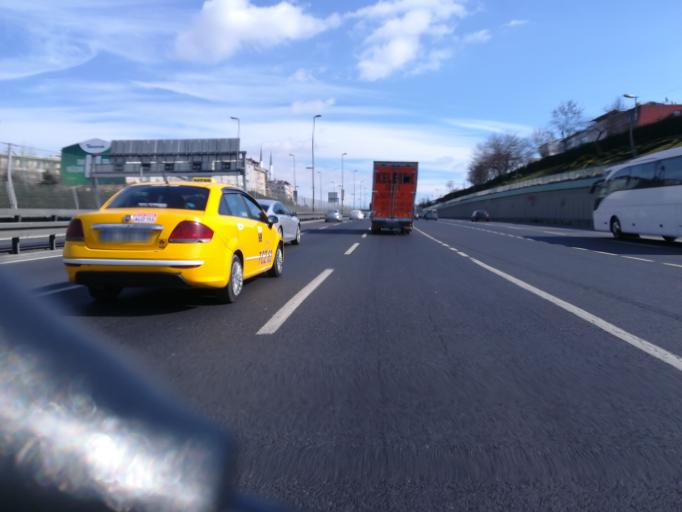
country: TR
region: Istanbul
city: Sisli
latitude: 41.0530
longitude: 28.9531
